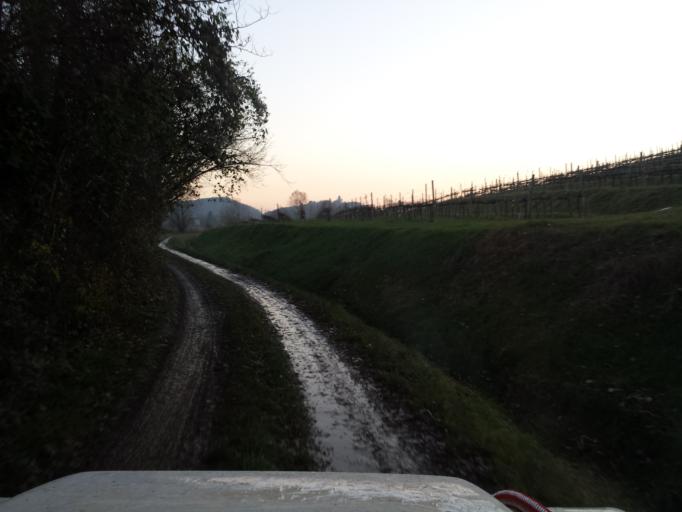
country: IT
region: Friuli Venezia Giulia
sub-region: Provincia di Udine
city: Corno di Rosazzo
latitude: 45.9983
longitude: 13.4626
